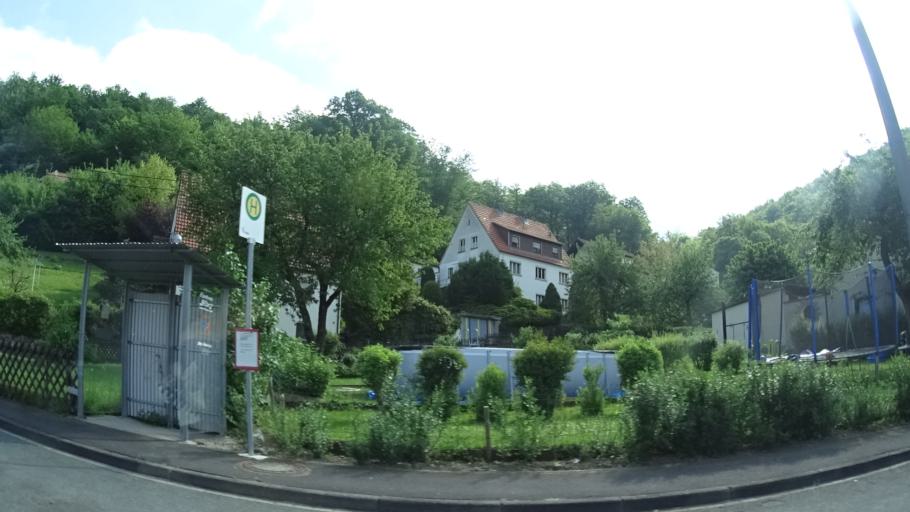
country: DE
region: Bavaria
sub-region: Regierungsbezirk Unterfranken
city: Schonau
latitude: 50.0743
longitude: 9.7236
